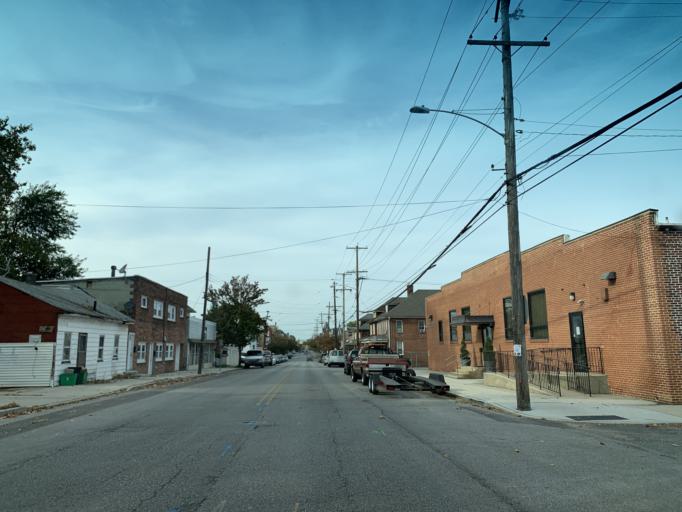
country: US
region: Pennsylvania
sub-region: York County
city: York
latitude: 39.9587
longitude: -76.7189
